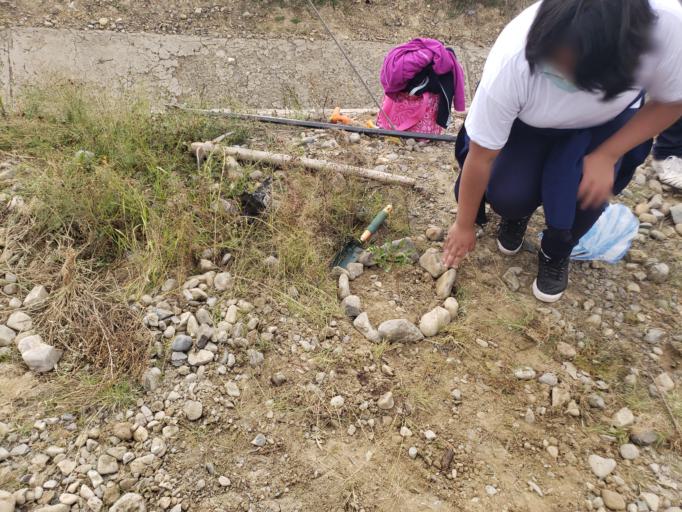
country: BO
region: La Paz
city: La Paz
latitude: -16.5790
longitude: -68.0758
